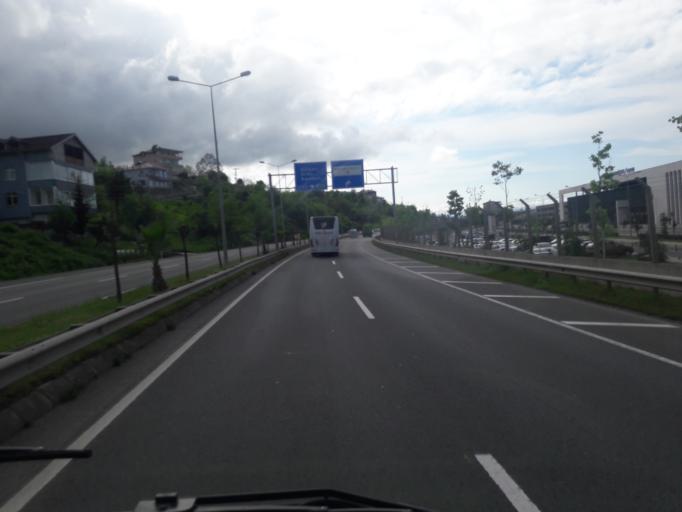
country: TR
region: Ordu
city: Gulyali
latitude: 40.9628
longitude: 38.0812
